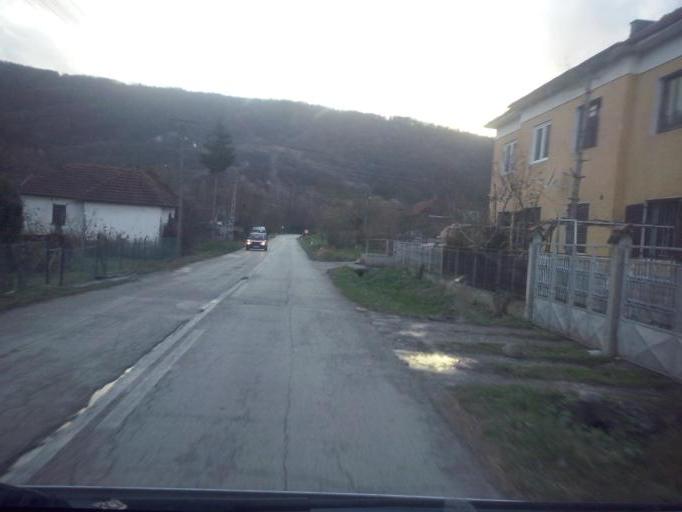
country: RS
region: Central Serbia
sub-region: Pirotski Okrug
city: Bela Palanka
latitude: 43.0351
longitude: 22.4058
